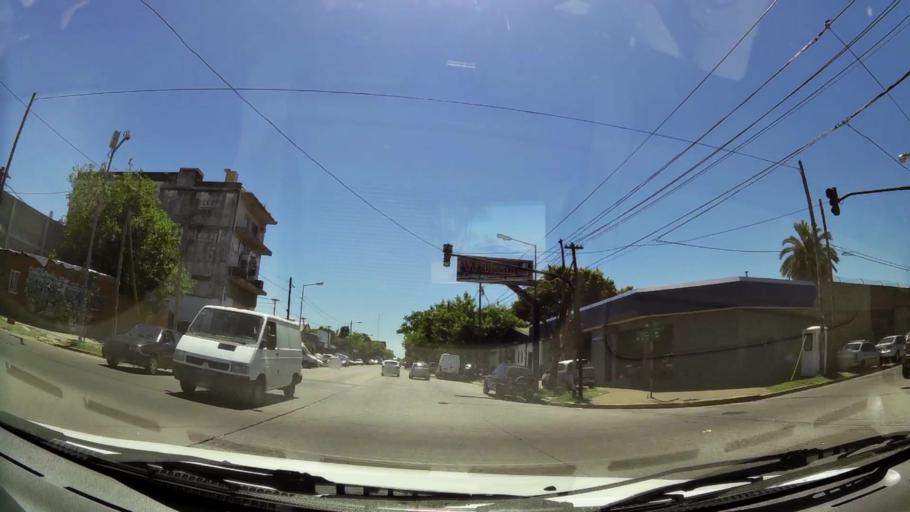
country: AR
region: Buenos Aires
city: Caseros
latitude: -34.5788
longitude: -58.5511
